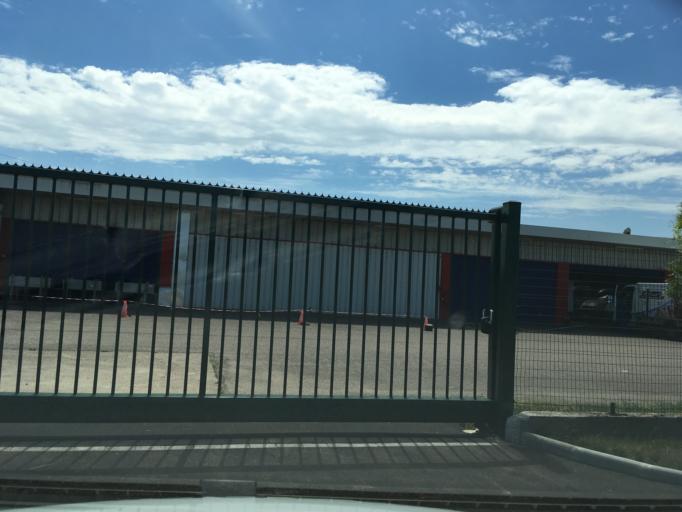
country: FR
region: Lorraine
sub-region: Departement de la Moselle
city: Metz
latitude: 49.1405
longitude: 6.1798
